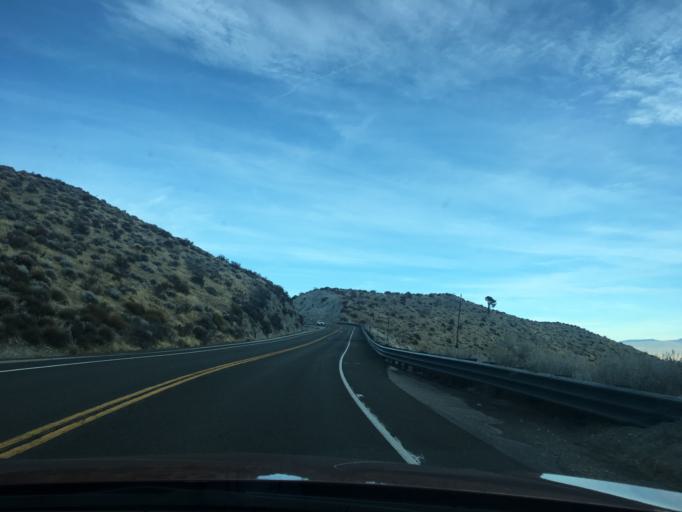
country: US
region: Nevada
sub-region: Douglas County
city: Kingsbury
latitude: 38.9500
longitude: -119.8492
